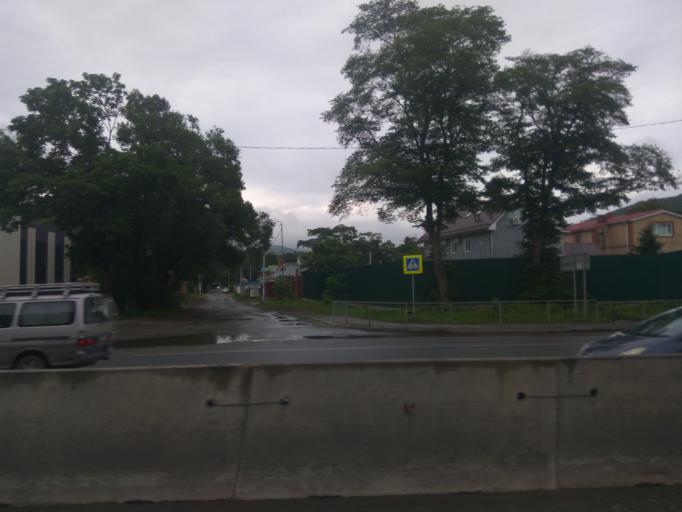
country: RU
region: Primorskiy
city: Trudovoye
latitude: 43.2182
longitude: 131.9607
